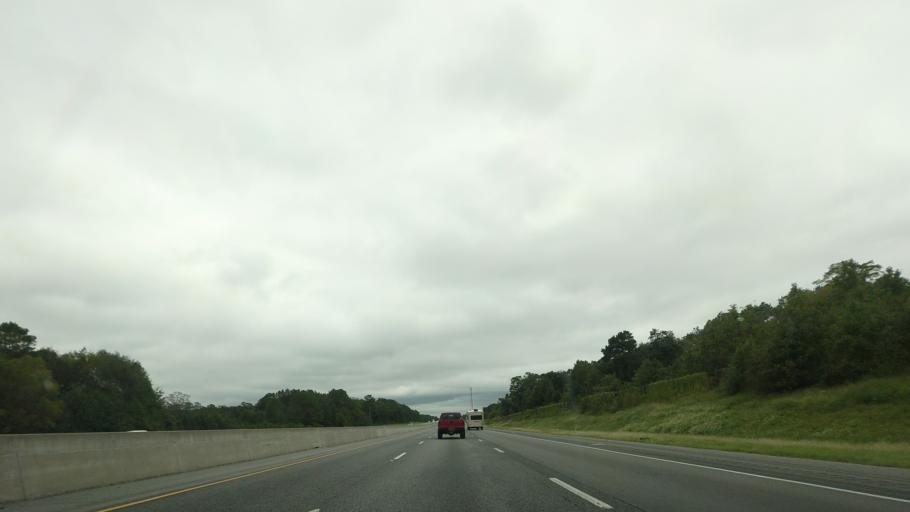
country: US
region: Georgia
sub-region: Lowndes County
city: Hahira
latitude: 30.9488
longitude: -83.3748
